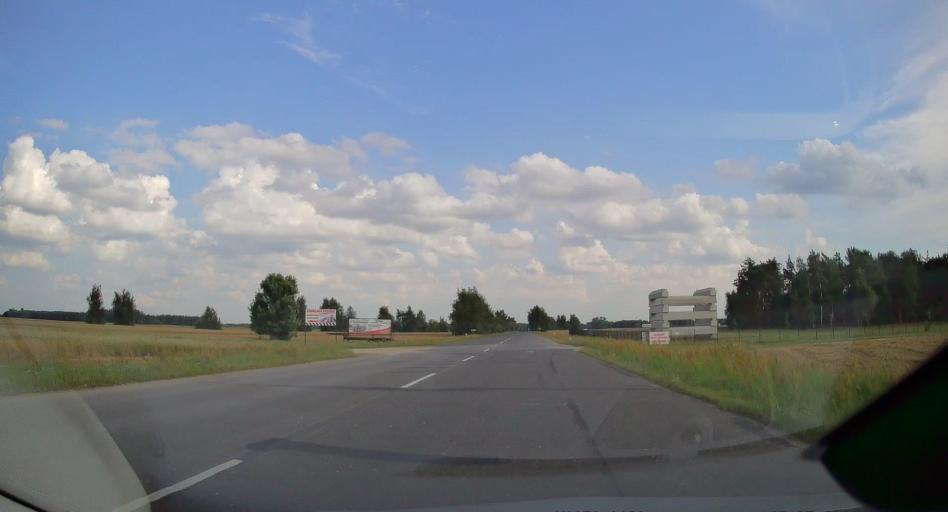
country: PL
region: Lodz Voivodeship
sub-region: Powiat tomaszowski
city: Rzeczyca
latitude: 51.6516
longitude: 20.2784
